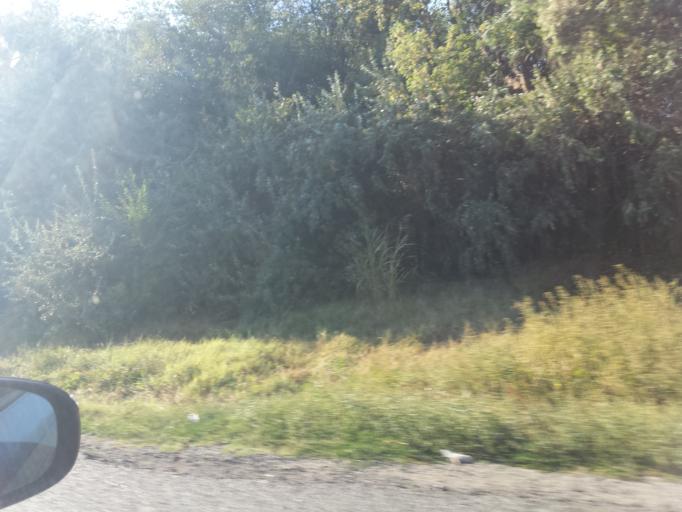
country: RO
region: Ialomita
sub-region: Comuna Slobozia
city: Slobozia
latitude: 44.5725
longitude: 27.3922
